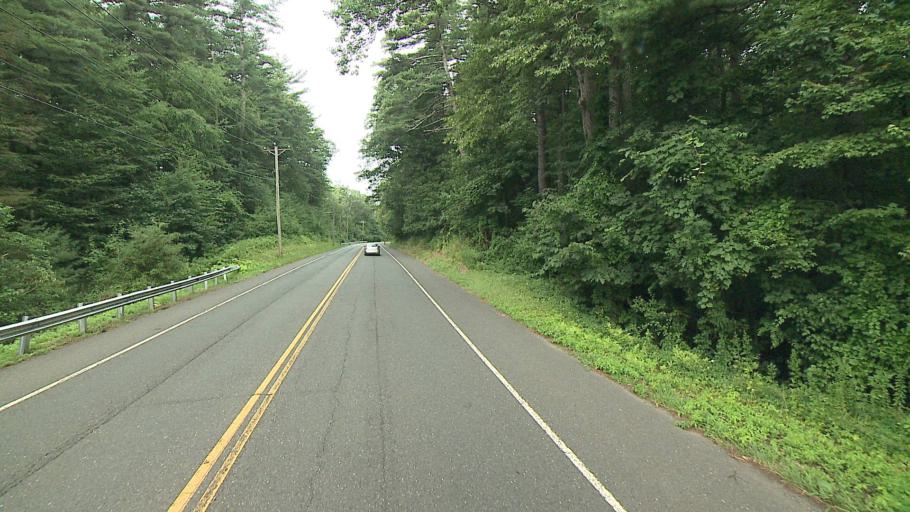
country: US
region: Connecticut
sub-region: New Haven County
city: Middlebury
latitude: 41.5243
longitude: -73.1651
